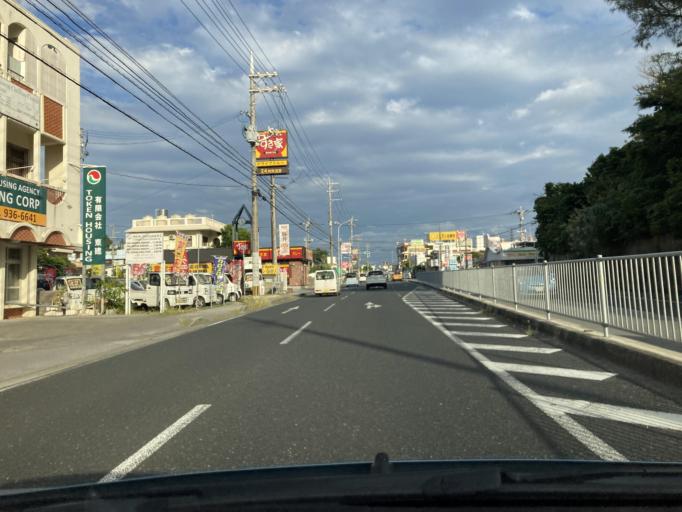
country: JP
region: Okinawa
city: Chatan
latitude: 26.3295
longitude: 127.7752
